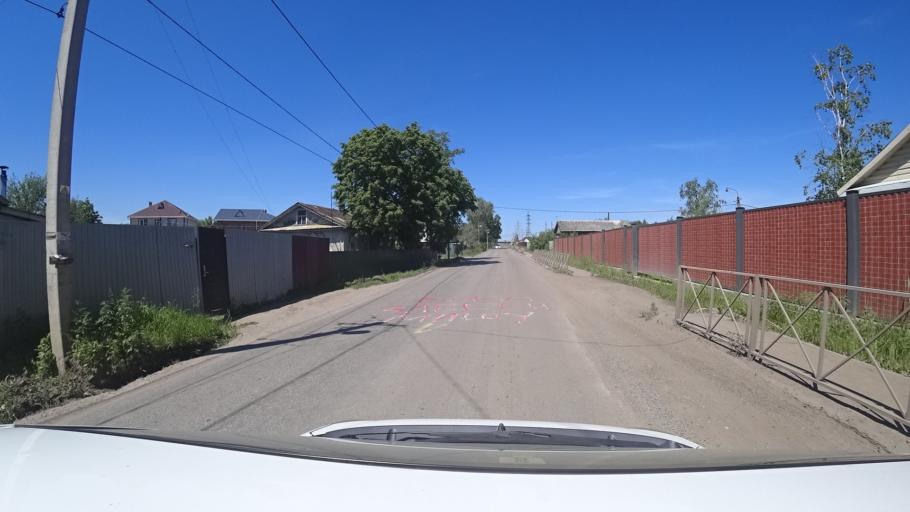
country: RU
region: Khabarovsk Krai
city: Topolevo
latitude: 48.4738
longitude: 135.1794
